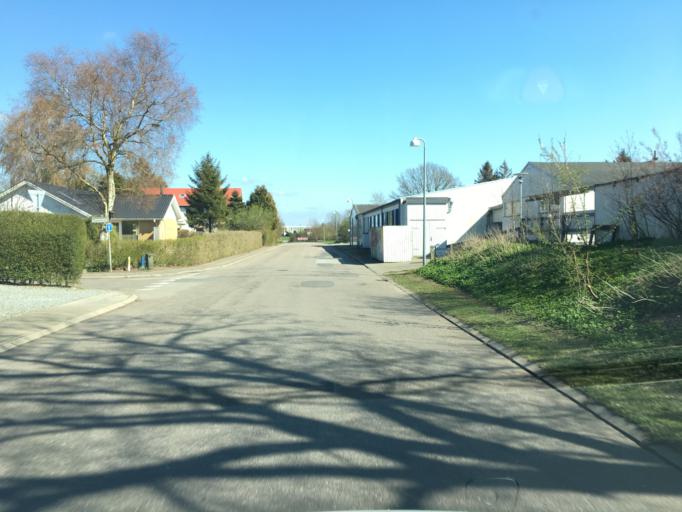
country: DK
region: South Denmark
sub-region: Aabenraa Kommune
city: Krusa
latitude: 54.9318
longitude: 9.4470
